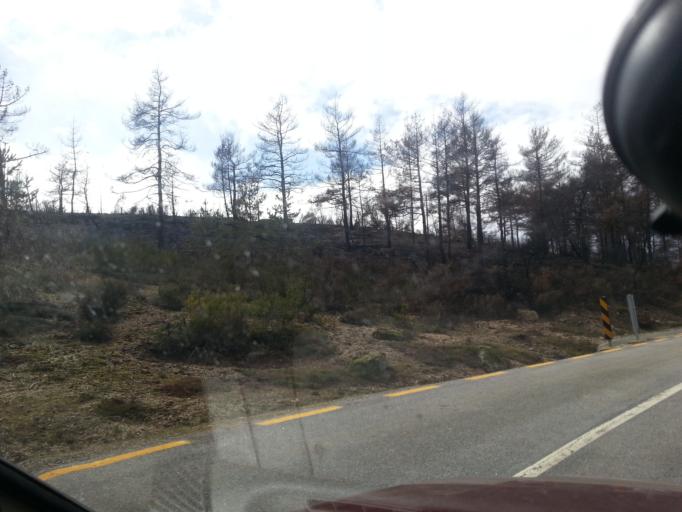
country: PT
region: Guarda
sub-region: Manteigas
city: Manteigas
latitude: 40.4199
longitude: -7.5975
